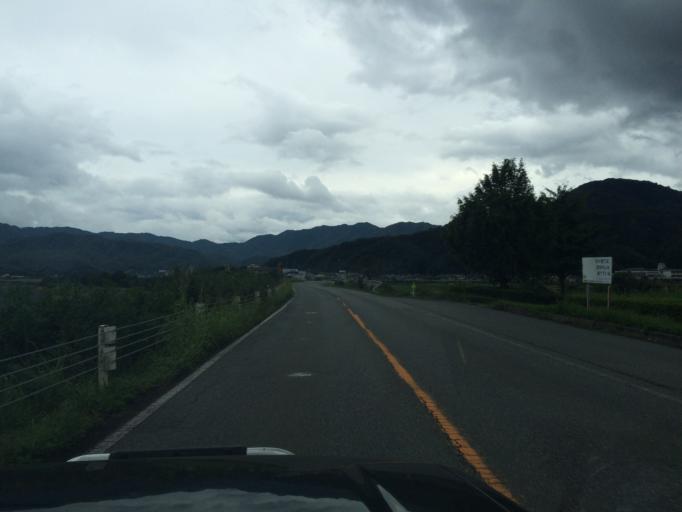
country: JP
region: Hyogo
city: Toyooka
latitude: 35.4456
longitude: 134.7735
